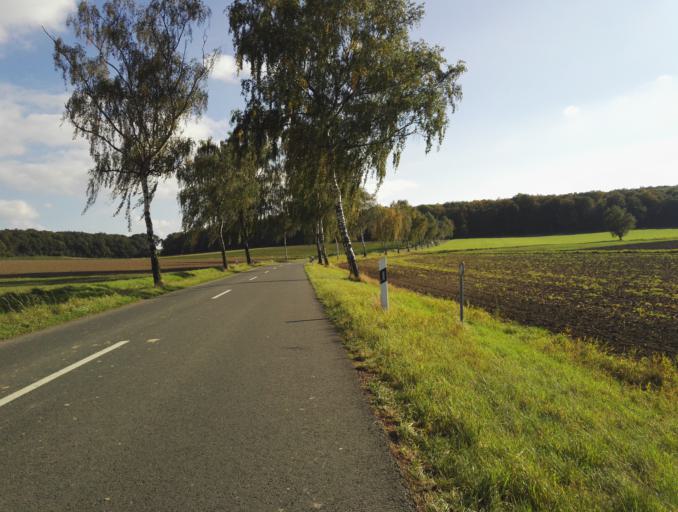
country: DE
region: Lower Saxony
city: Schellerten
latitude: 52.1415
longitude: 10.1350
